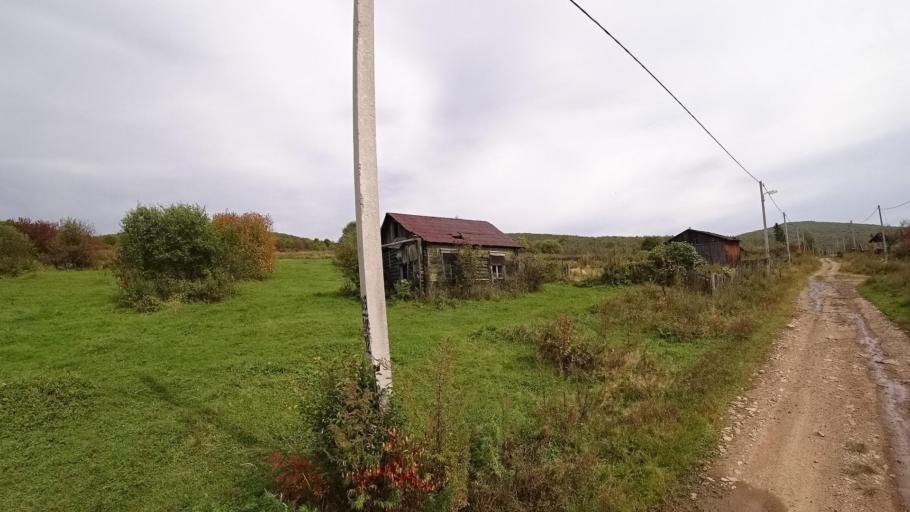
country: RU
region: Jewish Autonomous Oblast
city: Khingansk
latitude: 49.1226
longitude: 131.2076
